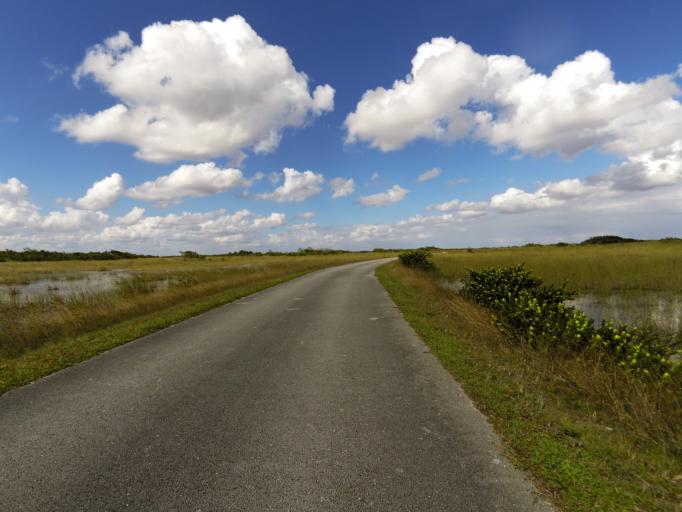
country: US
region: Florida
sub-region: Miami-Dade County
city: The Hammocks
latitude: 25.7070
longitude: -80.7619
